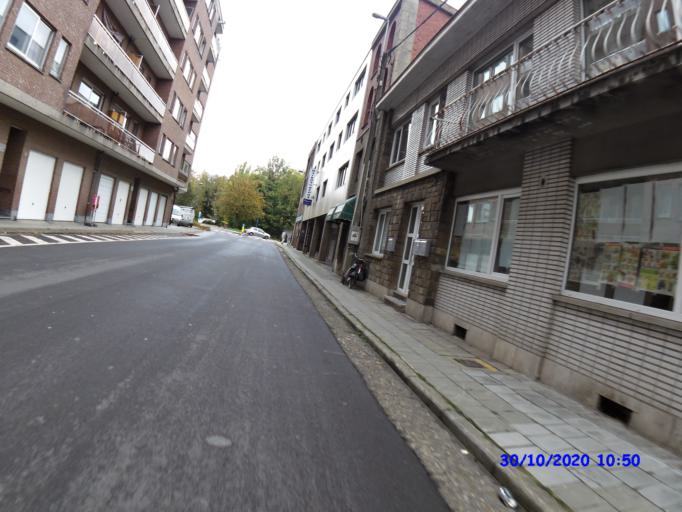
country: BE
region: Wallonia
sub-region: Province de Liege
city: Waremme
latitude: 50.6955
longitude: 5.2489
